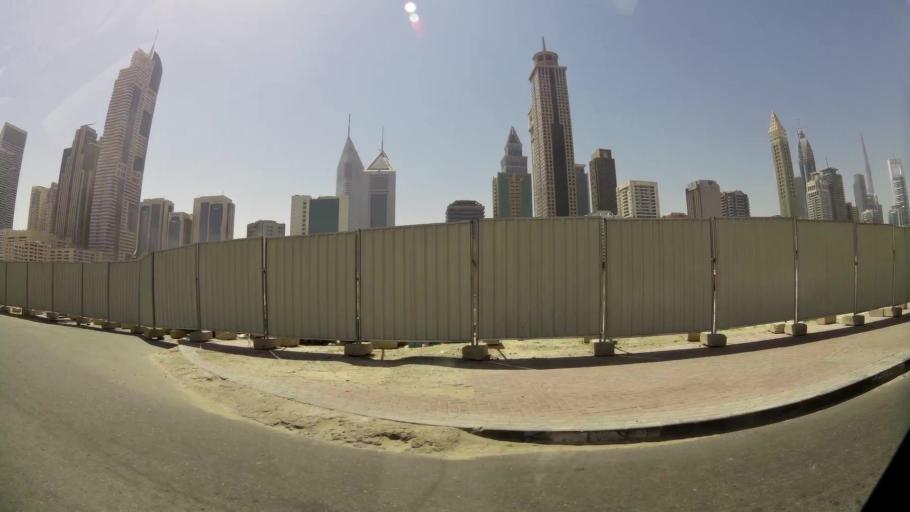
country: AE
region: Ash Shariqah
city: Sharjah
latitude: 25.2207
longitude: 55.2757
